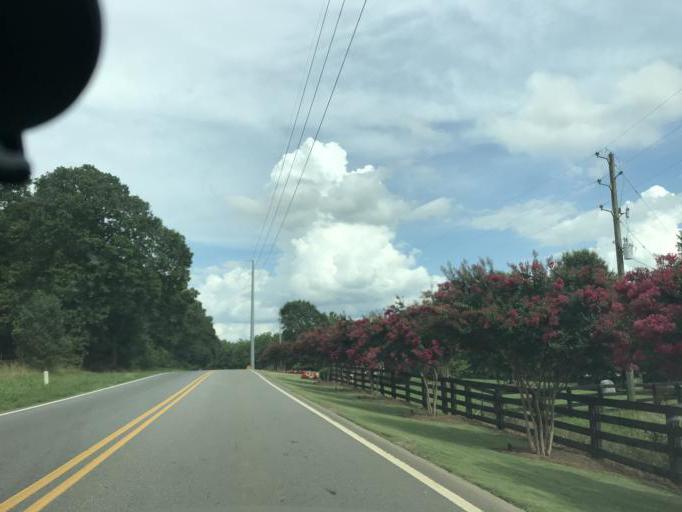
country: US
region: Georgia
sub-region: Cherokee County
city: Ball Ground
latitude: 34.3120
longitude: -84.2379
